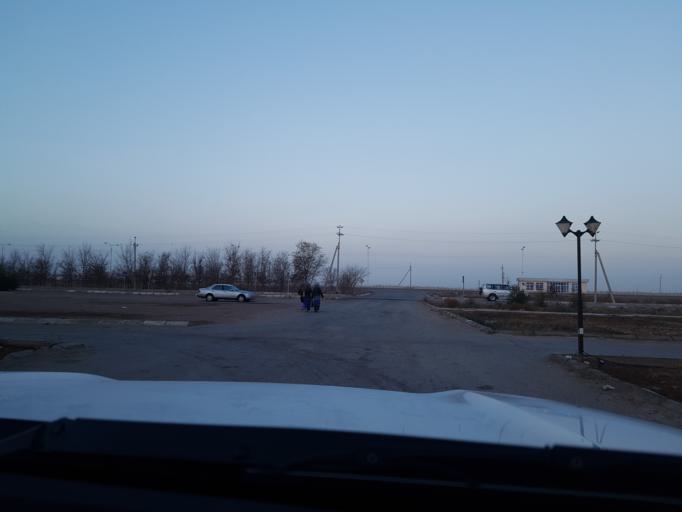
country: TM
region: Dasoguz
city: Koeneuergench
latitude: 41.7415
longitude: 58.6891
